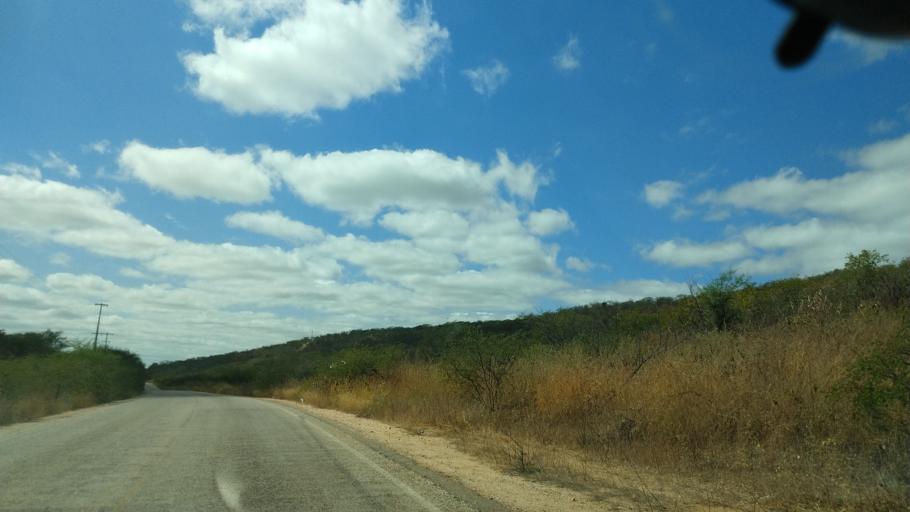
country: BR
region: Rio Grande do Norte
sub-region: Currais Novos
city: Currais Novos
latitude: -6.2619
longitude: -36.5814
